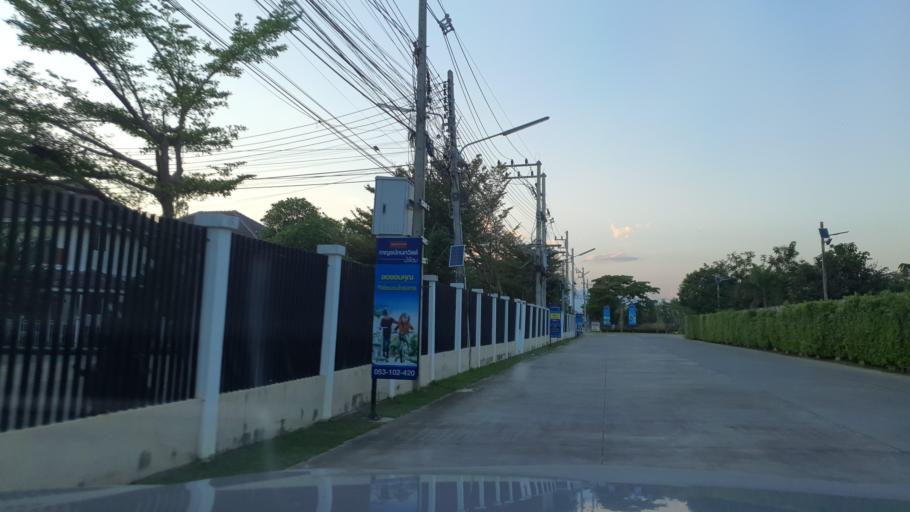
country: TH
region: Chiang Mai
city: Saraphi
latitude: 18.7321
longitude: 99.0748
